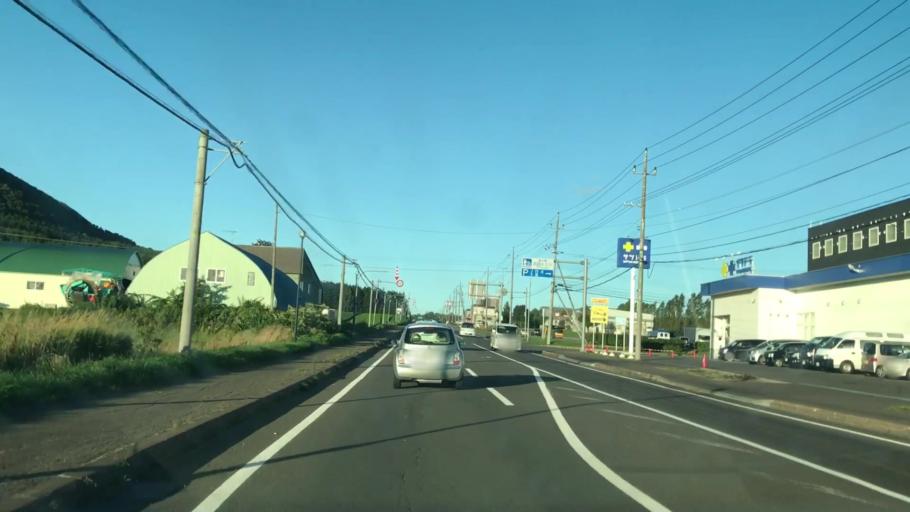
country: JP
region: Hokkaido
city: Niseko Town
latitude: 42.7402
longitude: 140.8825
